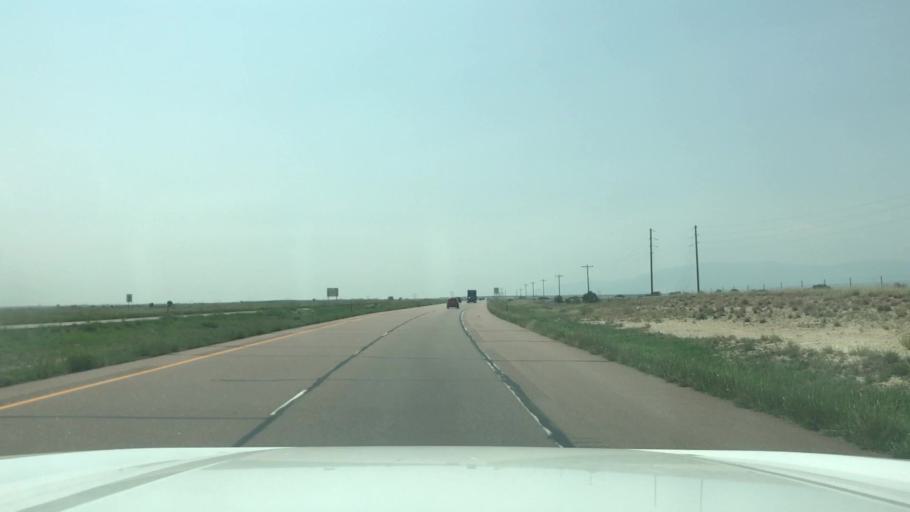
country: US
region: Colorado
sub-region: Pueblo County
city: Pueblo
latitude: 38.1114
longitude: -104.6760
